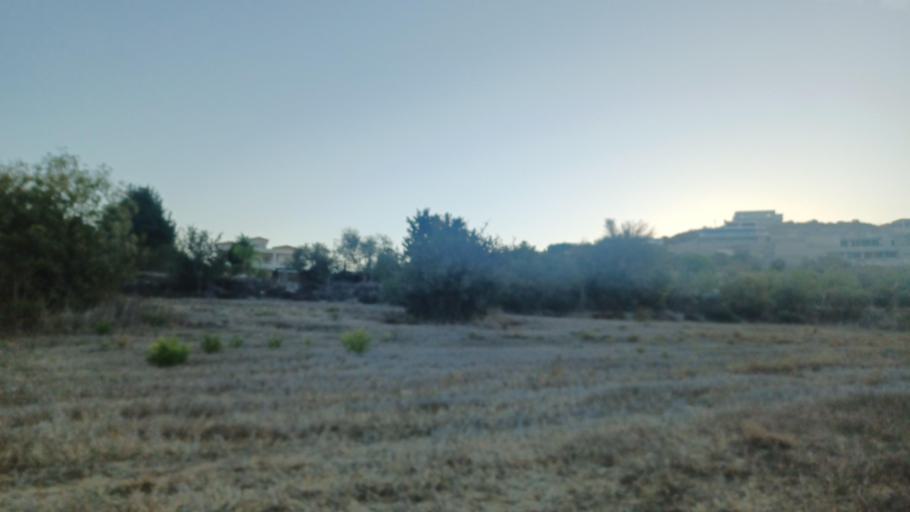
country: CY
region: Pafos
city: Mesogi
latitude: 34.7892
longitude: 32.4685
